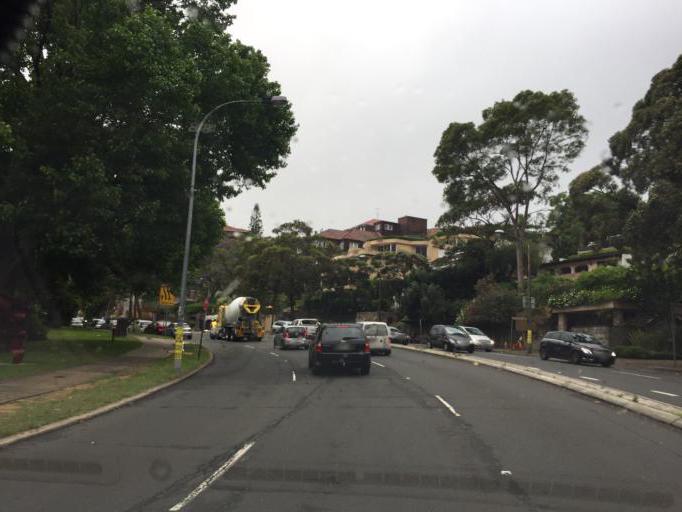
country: AU
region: New South Wales
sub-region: Woollahra
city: Bellevue Hill
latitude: -33.8750
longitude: 151.2469
